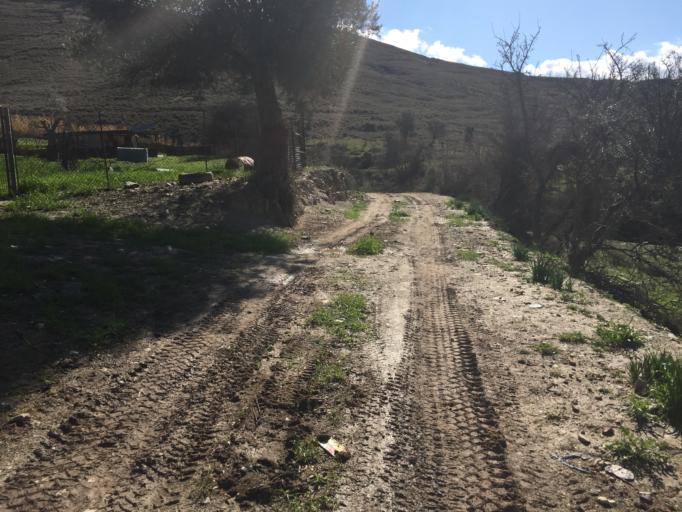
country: CY
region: Limassol
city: Pachna
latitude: 34.8760
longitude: 32.6768
